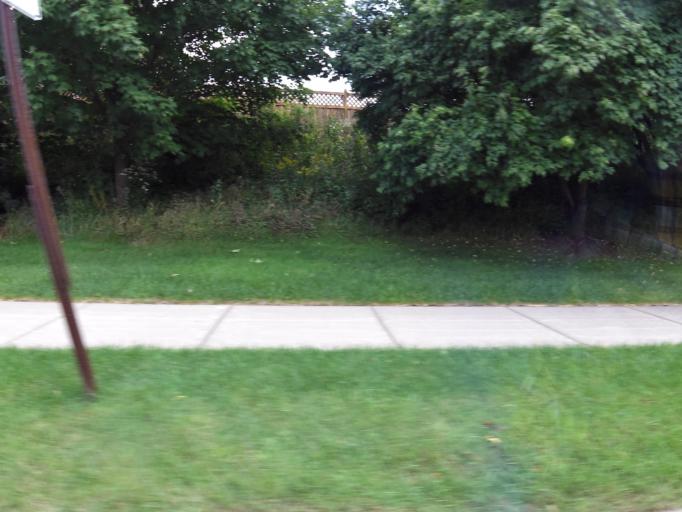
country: US
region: Minnesota
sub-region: Dakota County
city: Inver Grove Heights
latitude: 44.8203
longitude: -93.0409
